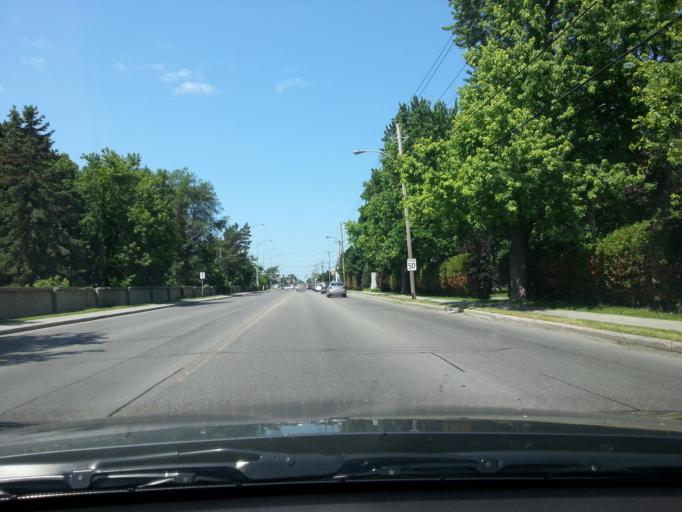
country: CA
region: Ontario
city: Bells Corners
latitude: 45.3961
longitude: -75.8278
